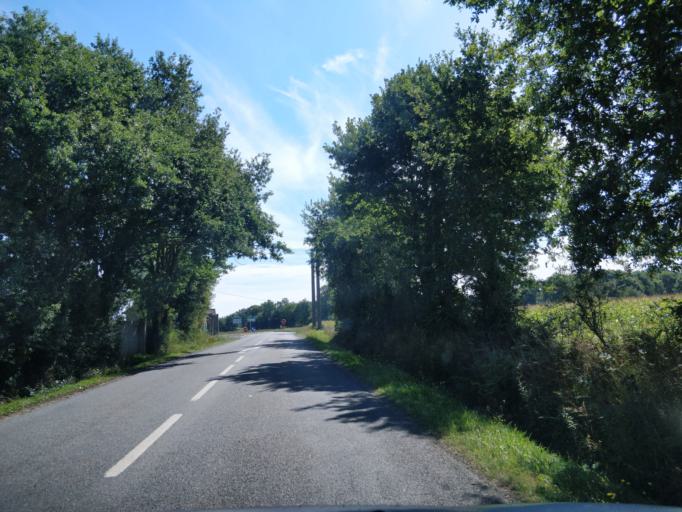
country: FR
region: Pays de la Loire
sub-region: Departement de la Loire-Atlantique
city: Derval
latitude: 47.6872
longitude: -1.6876
